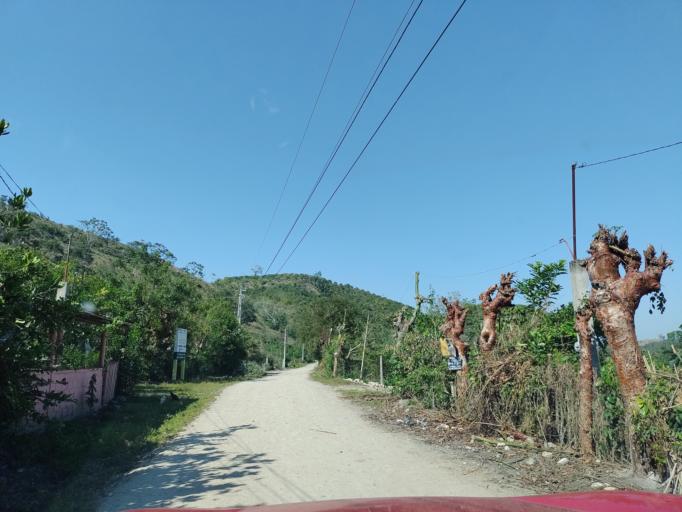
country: MX
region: Veracruz
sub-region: Papantla
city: Polutla
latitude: 20.4963
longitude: -97.1787
